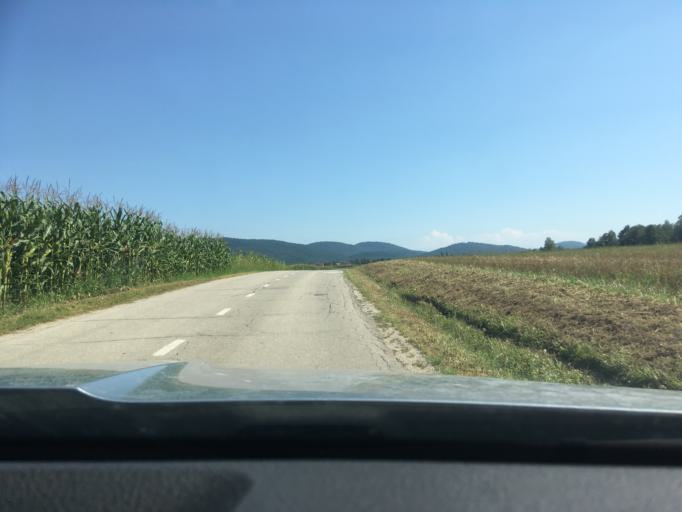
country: SI
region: Metlika
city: Metlika
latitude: 45.5844
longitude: 15.2839
